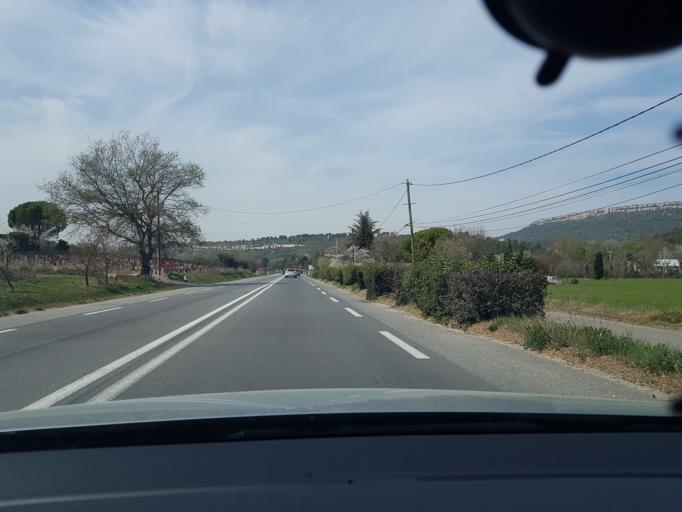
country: FR
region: Provence-Alpes-Cote d'Azur
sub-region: Departement des Bouches-du-Rhone
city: Chateauneuf-le-Rouge
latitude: 43.4750
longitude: 5.5749
